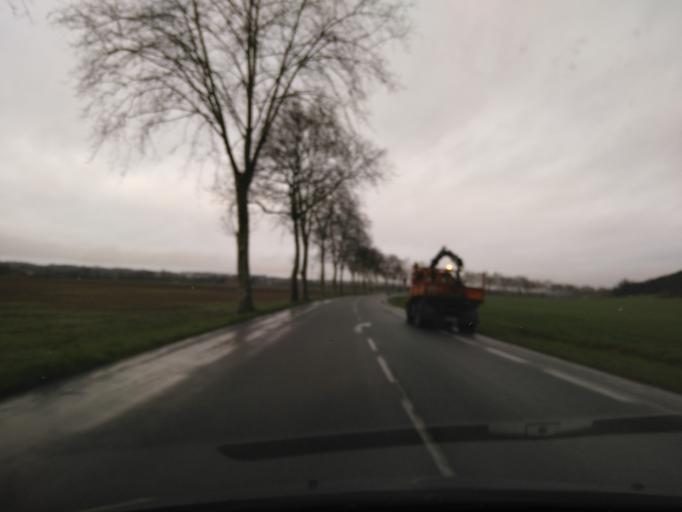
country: FR
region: Midi-Pyrenees
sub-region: Departement de la Haute-Garonne
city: Rieux-Volvestre
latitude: 43.2368
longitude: 1.2055
